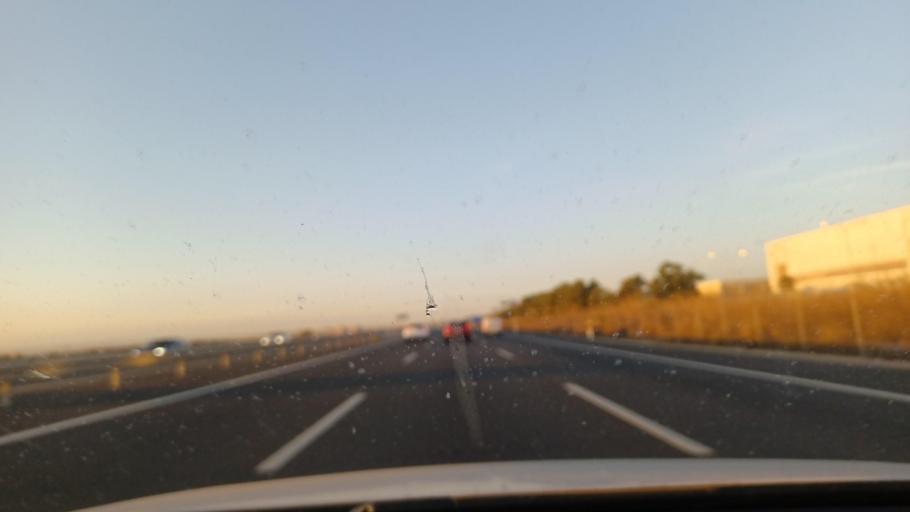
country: ES
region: Valencia
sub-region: Provincia de Valencia
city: Albuixech
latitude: 39.5431
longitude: -0.3020
